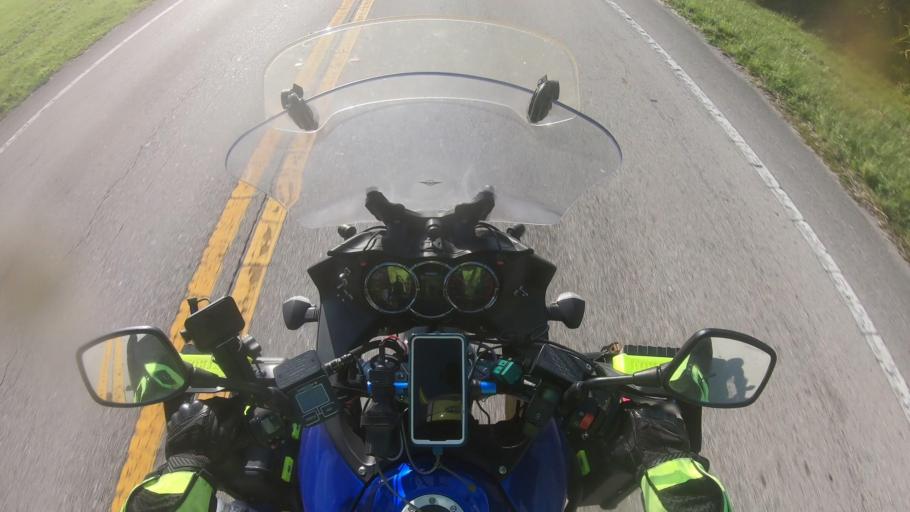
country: US
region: Florida
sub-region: Highlands County
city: Placid Lakes
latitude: 27.2095
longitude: -81.3922
